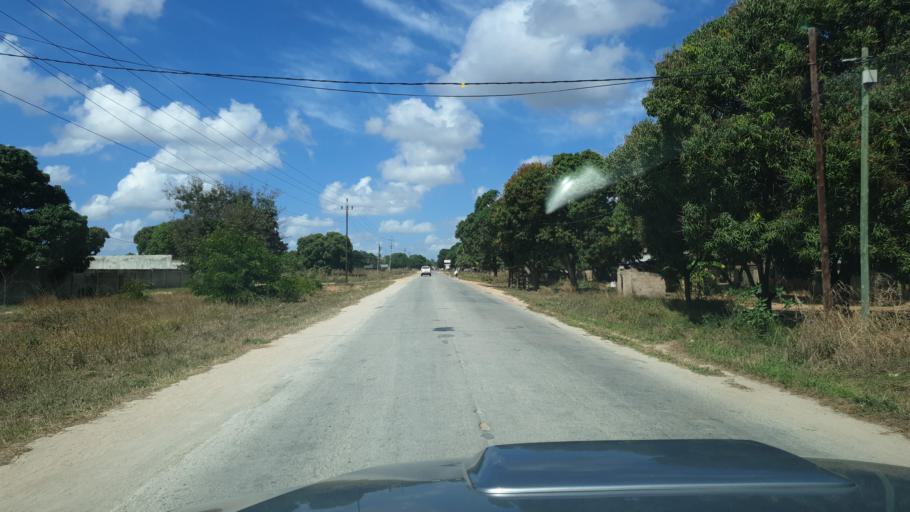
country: MZ
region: Nampula
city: Nacala
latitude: -14.5031
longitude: 40.6972
